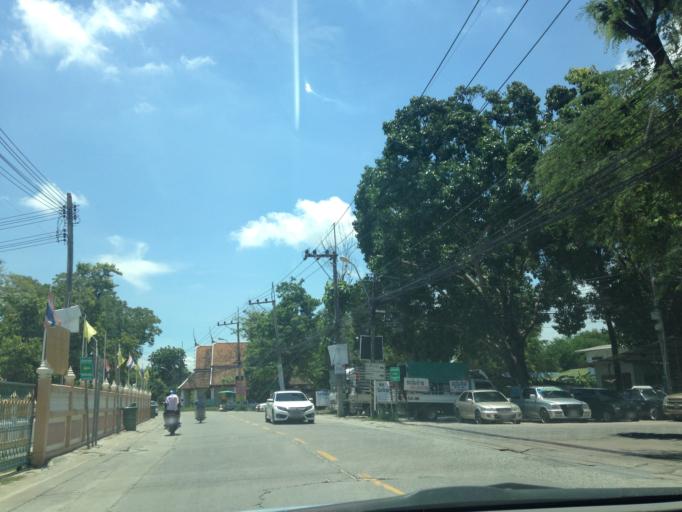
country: TH
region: Chon Buri
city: Chon Buri
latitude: 13.2937
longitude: 100.9372
